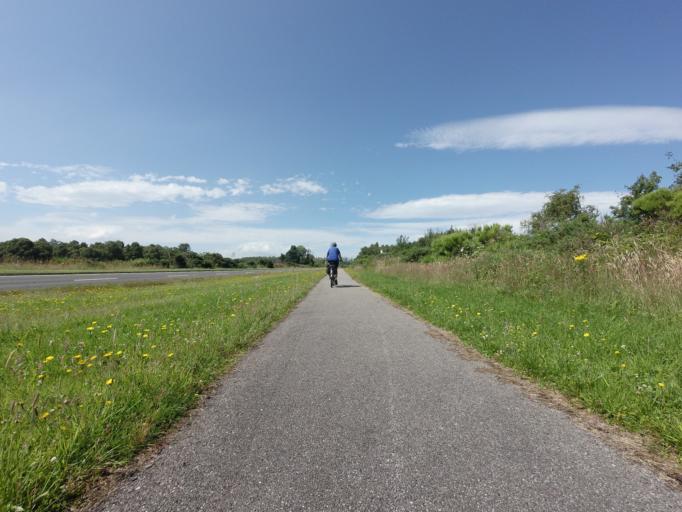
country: GB
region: Scotland
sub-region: Highland
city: Conon Bridge
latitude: 57.5387
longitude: -4.3676
